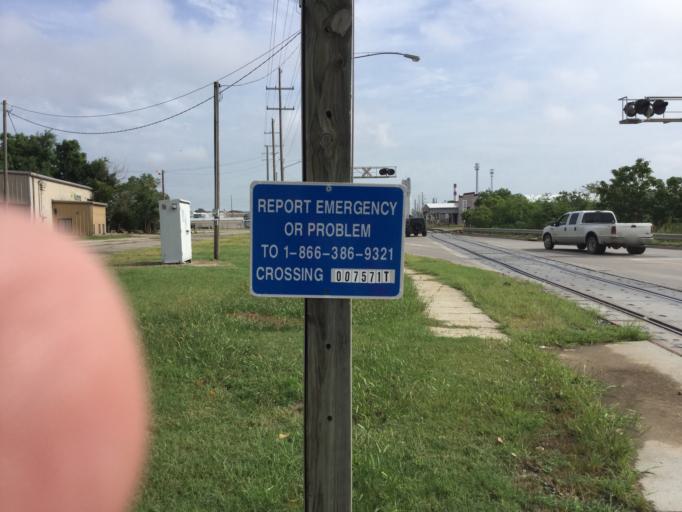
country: US
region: Kansas
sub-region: Montgomery County
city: Coffeyville
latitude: 37.0289
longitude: -95.6159
